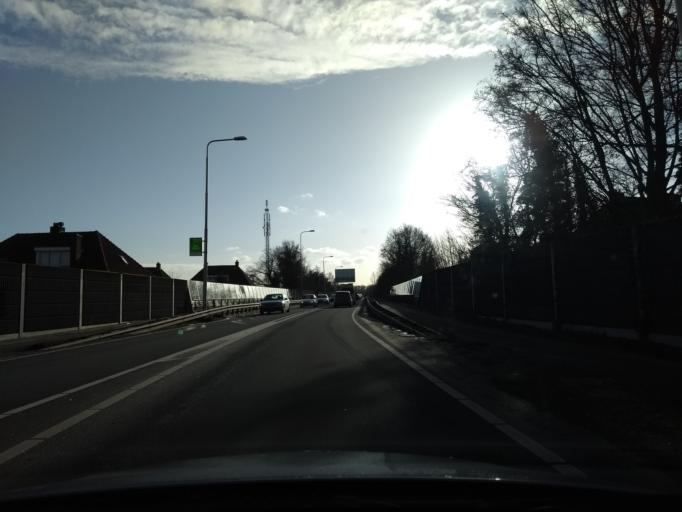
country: NL
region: Overijssel
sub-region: Gemeente Almelo
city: Almelo
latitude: 52.3657
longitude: 6.6717
